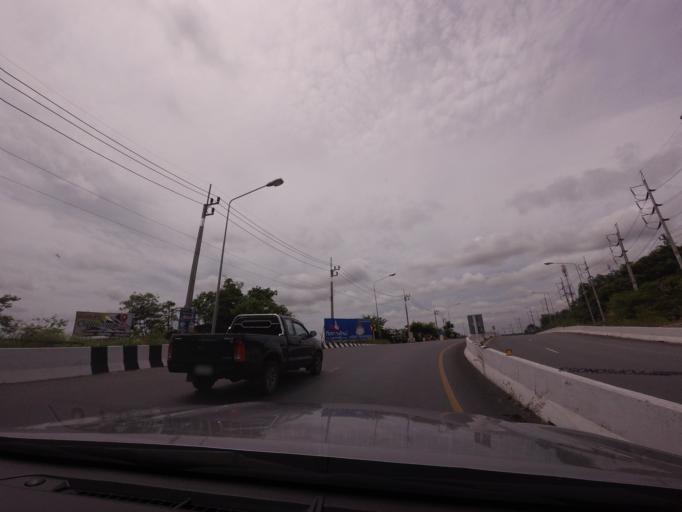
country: TH
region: Nakhon Si Thammarat
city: Hua Sai
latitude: 8.0615
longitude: 100.2031
